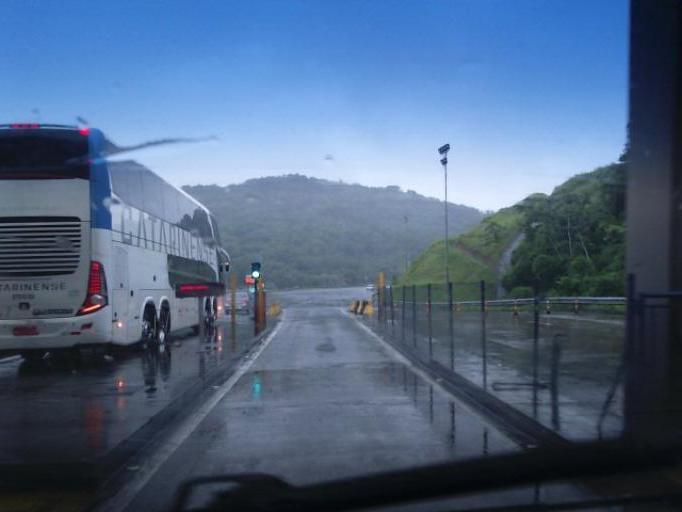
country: BR
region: Sao Paulo
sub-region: Juquia
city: Juquia
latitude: -24.3894
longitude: -47.7221
